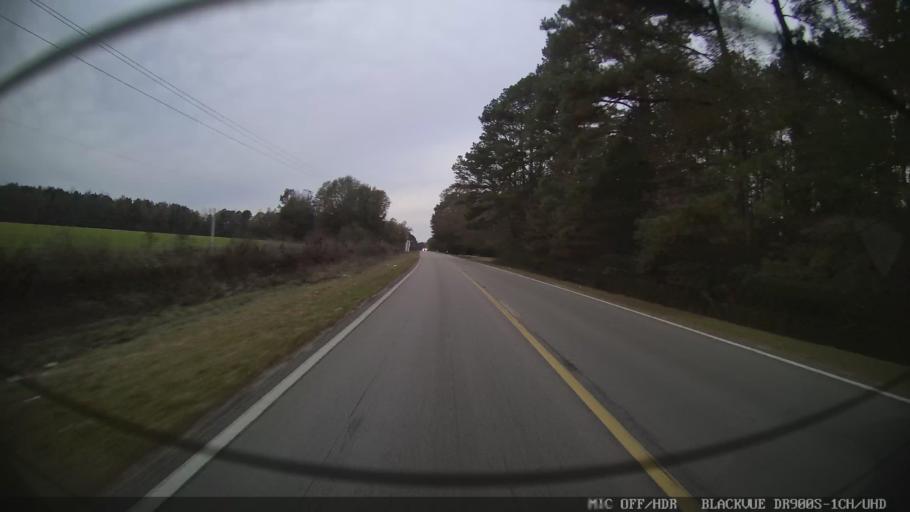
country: US
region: Mississippi
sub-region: Clarke County
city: Stonewall
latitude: 32.0238
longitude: -88.8535
